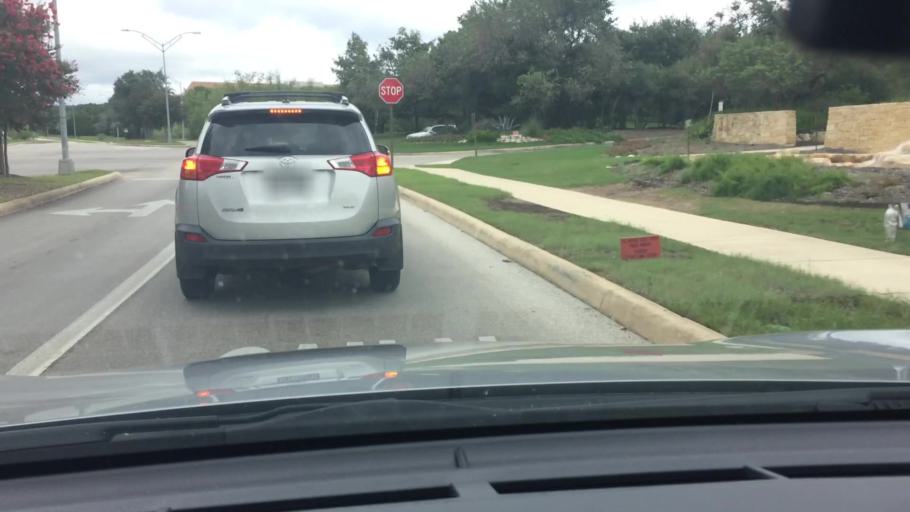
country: US
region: Texas
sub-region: Bexar County
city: Timberwood Park
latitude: 29.6620
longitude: -98.4010
